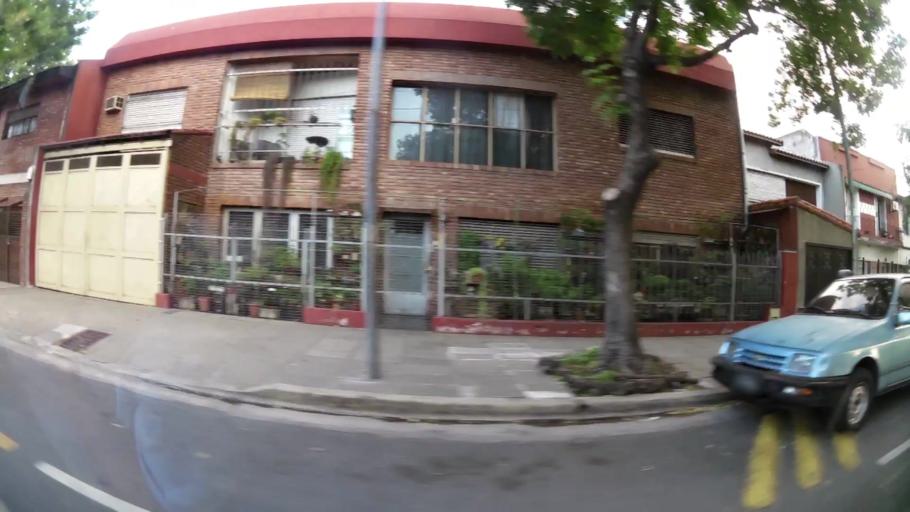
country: AR
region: Buenos Aires
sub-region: Partido de General San Martin
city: General San Martin
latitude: -34.5834
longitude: -58.5154
